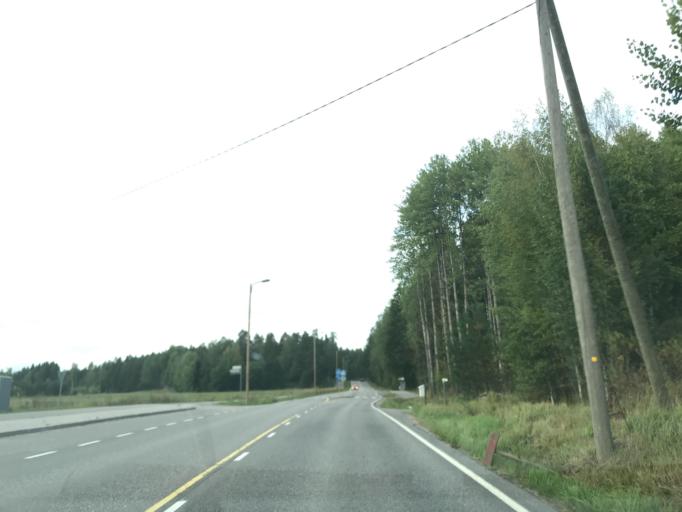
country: FI
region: Uusimaa
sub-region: Helsinki
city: Kirkkonummi
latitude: 60.2579
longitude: 24.4472
